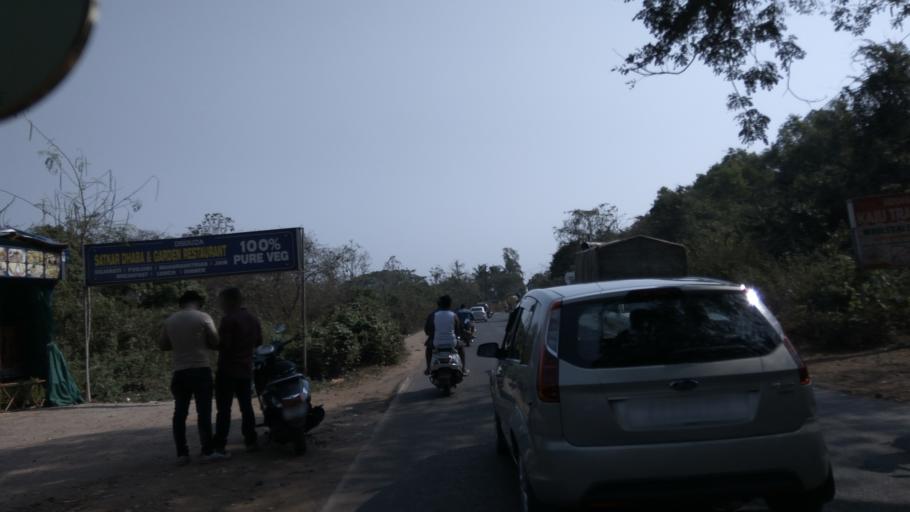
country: IN
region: Goa
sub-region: North Goa
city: Saligao
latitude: 15.5424
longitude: 73.7768
